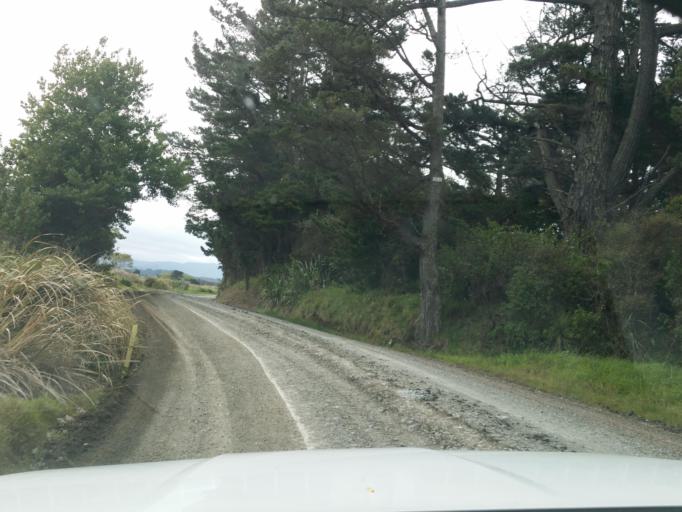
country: NZ
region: Northland
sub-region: Kaipara District
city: Dargaville
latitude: -35.9171
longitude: 173.9208
